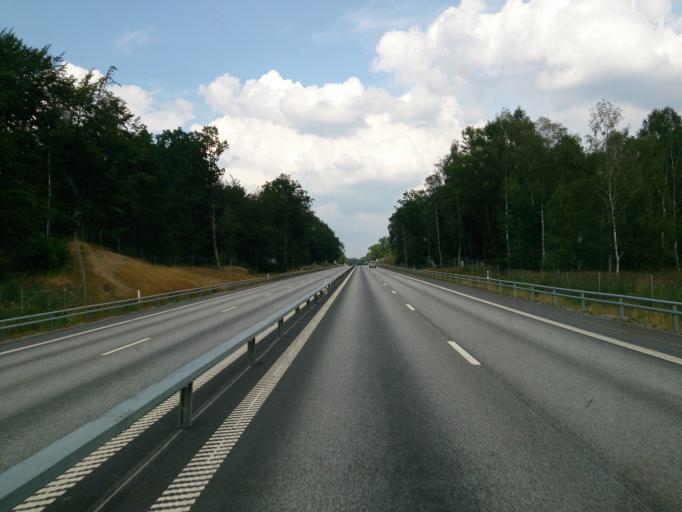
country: SE
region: Skane
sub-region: Horby Kommun
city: Hoerby
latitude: 55.9163
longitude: 13.7773
